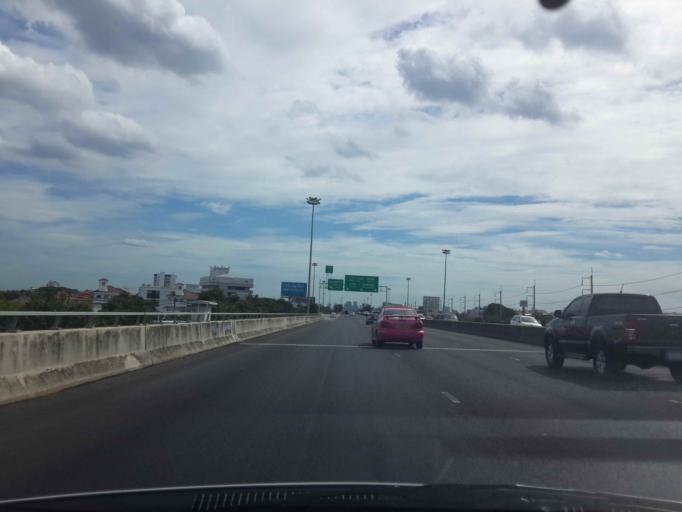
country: TH
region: Bangkok
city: Lat Phrao
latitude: 13.7990
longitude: 100.6145
